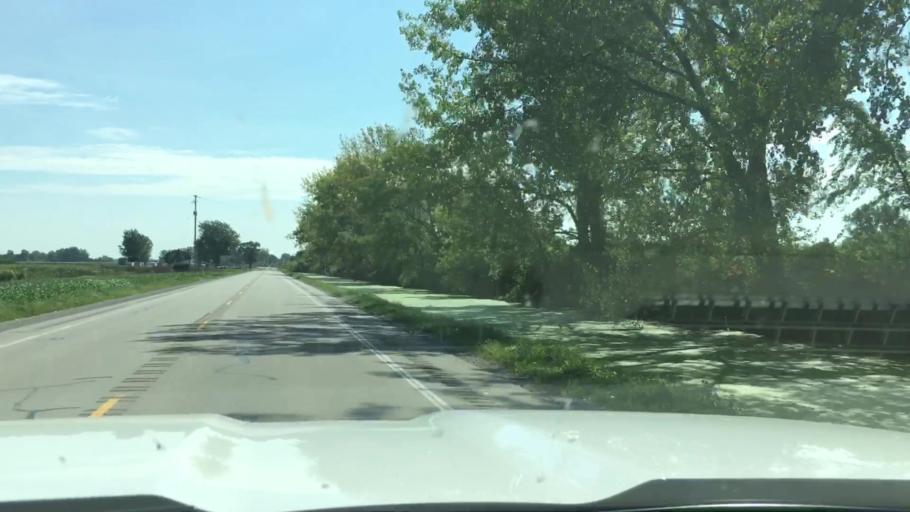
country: US
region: Michigan
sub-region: Tuscola County
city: Reese
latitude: 43.5823
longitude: -83.7077
